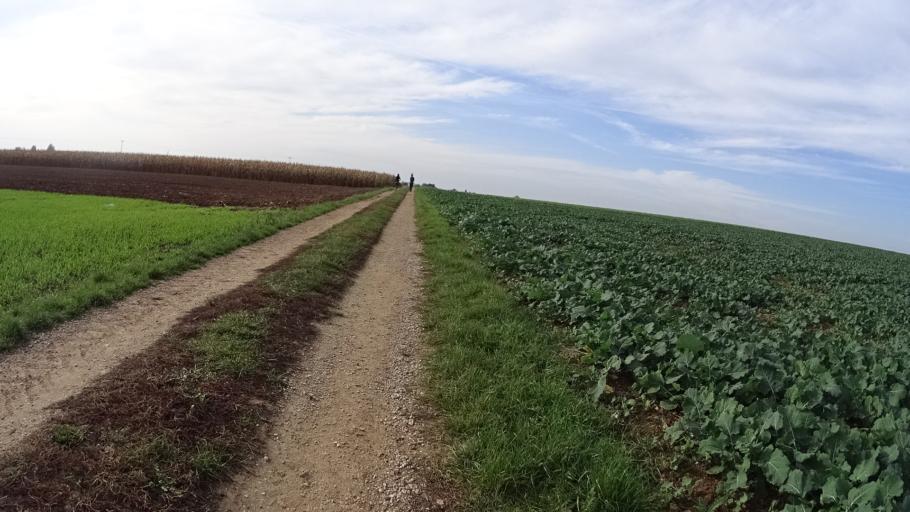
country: DE
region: Bavaria
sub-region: Upper Bavaria
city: Buxheim
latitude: 48.8206
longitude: 11.2903
